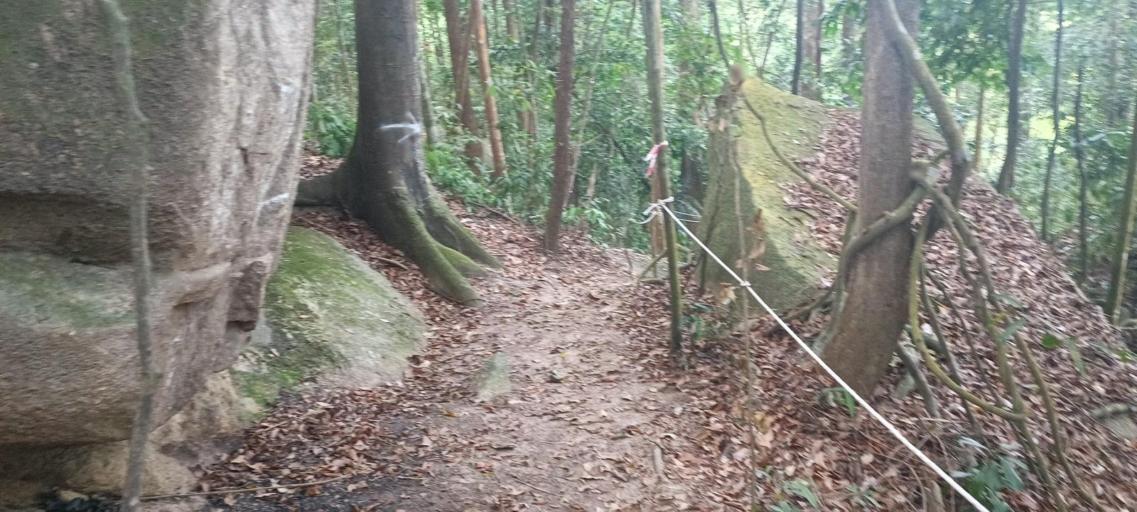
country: MY
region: Penang
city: Juru
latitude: 5.3349
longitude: 100.4109
